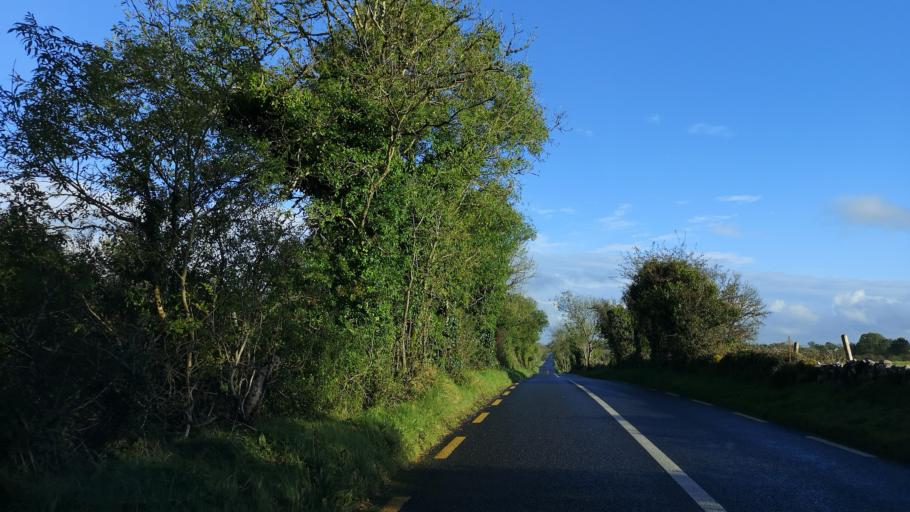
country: IE
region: Connaught
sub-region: Roscommon
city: Castlerea
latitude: 53.8200
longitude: -8.5456
